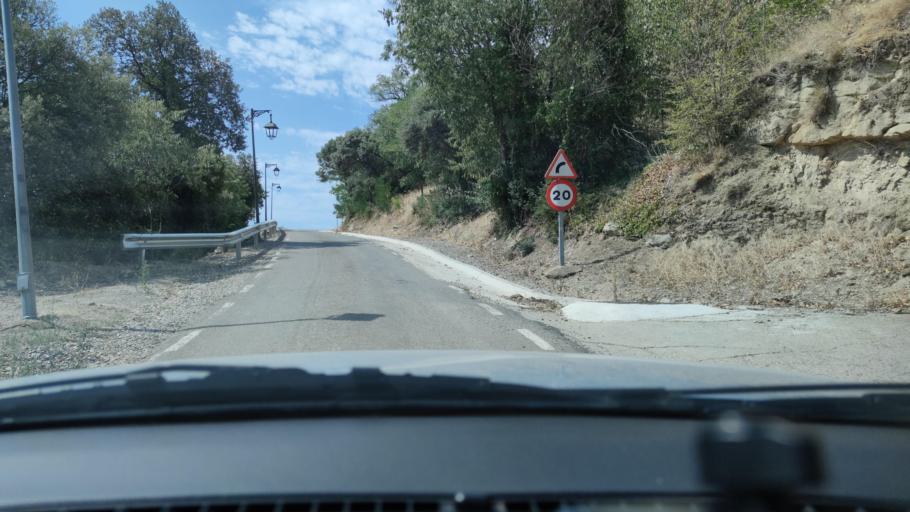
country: ES
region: Catalonia
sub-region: Provincia de Lleida
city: Ager
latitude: 42.0135
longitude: 0.8263
